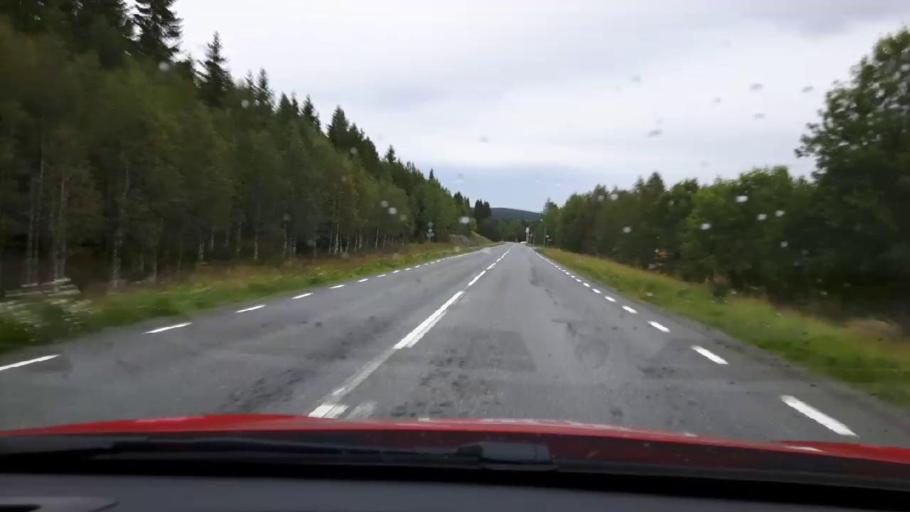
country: SE
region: Jaemtland
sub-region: Are Kommun
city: Jarpen
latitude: 63.3942
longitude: 13.3829
